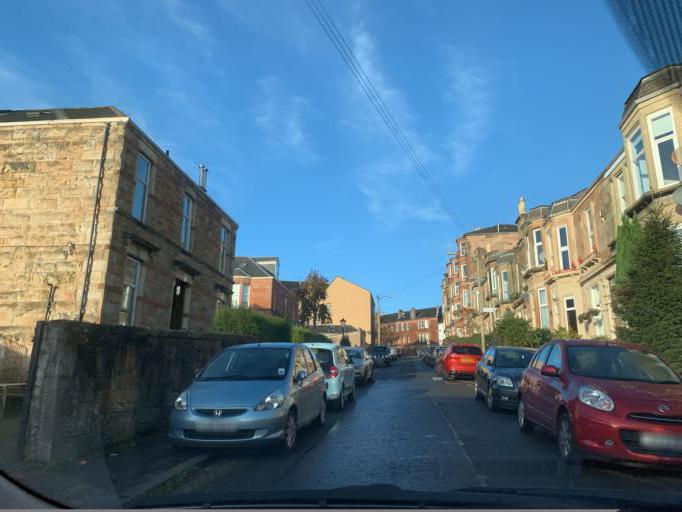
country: GB
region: Scotland
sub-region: East Renfrewshire
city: Giffnock
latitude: 55.8264
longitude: -4.2689
